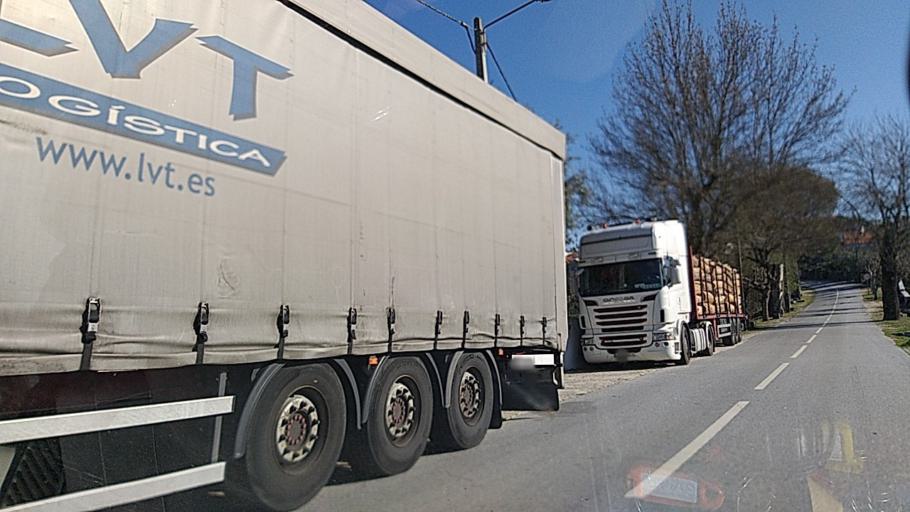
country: PT
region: Guarda
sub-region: Fornos de Algodres
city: Fornos de Algodres
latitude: 40.6269
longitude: -7.5013
